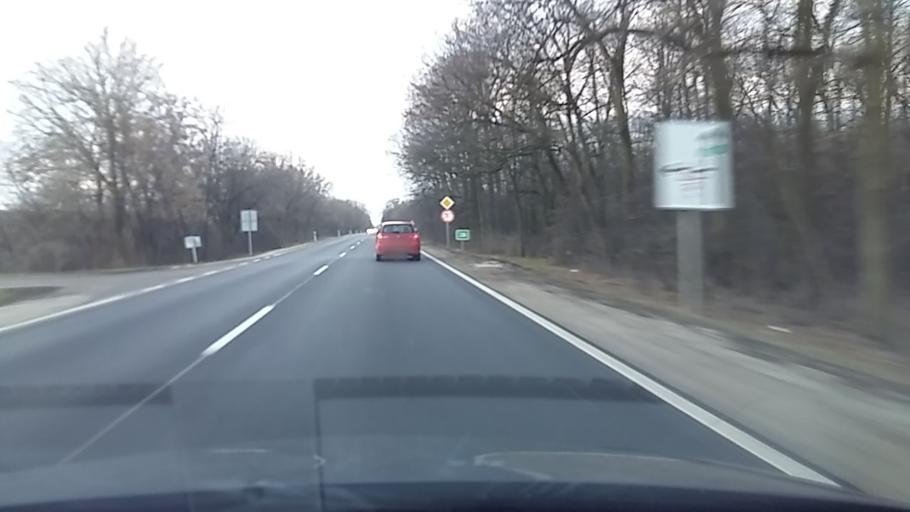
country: HU
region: Hajdu-Bihar
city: Debrecen
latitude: 47.5687
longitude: 21.6525
